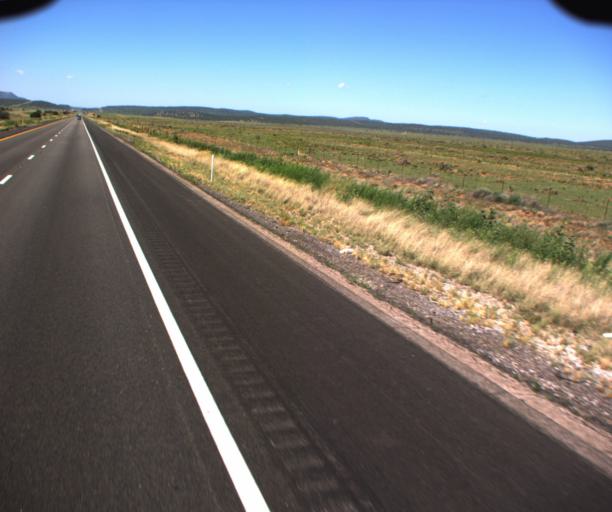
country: US
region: Arizona
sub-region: Mohave County
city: Peach Springs
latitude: 35.2720
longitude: -113.1427
